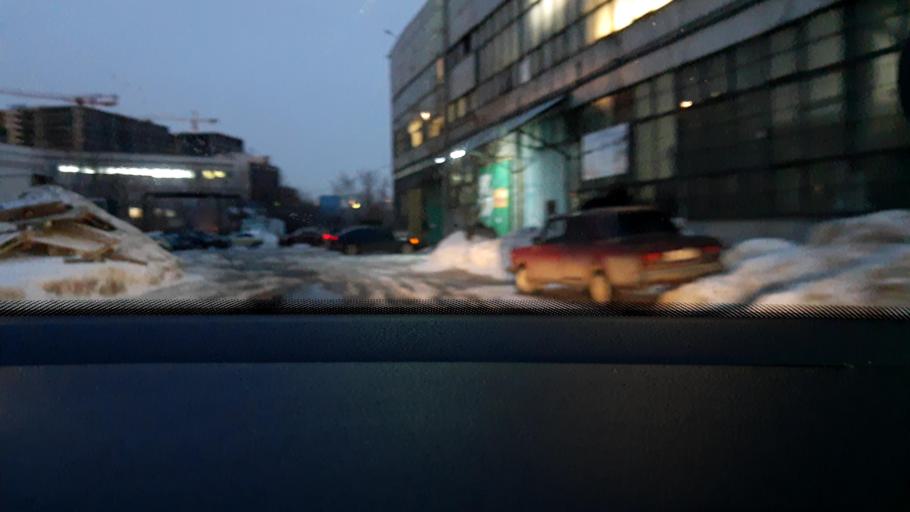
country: RU
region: Moscow
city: Tsaritsyno
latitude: 55.6077
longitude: 37.6477
